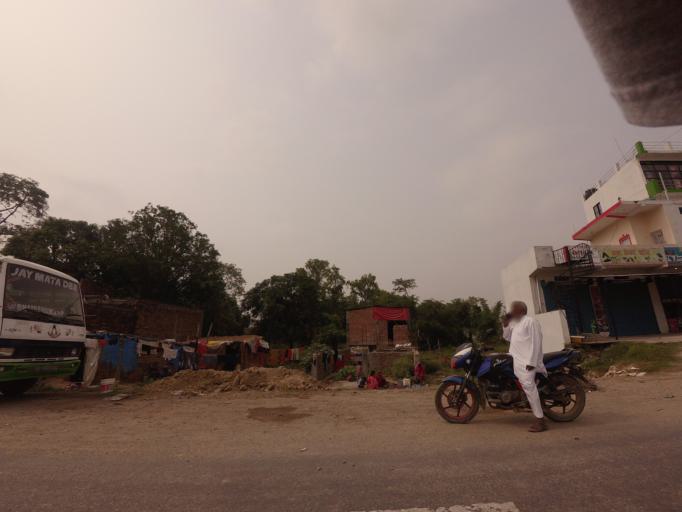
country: IN
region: Uttar Pradesh
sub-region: Maharajganj
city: Nautanwa
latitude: 27.4916
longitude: 83.3064
